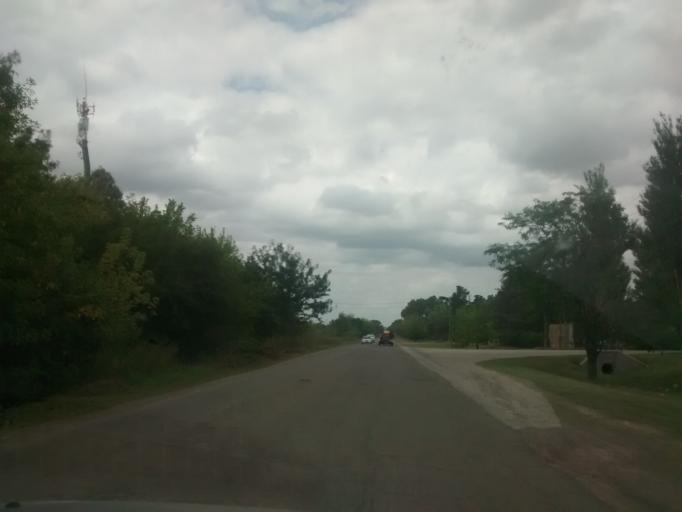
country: AR
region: Buenos Aires
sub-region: Partido de La Plata
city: La Plata
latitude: -34.9736
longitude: -57.9402
